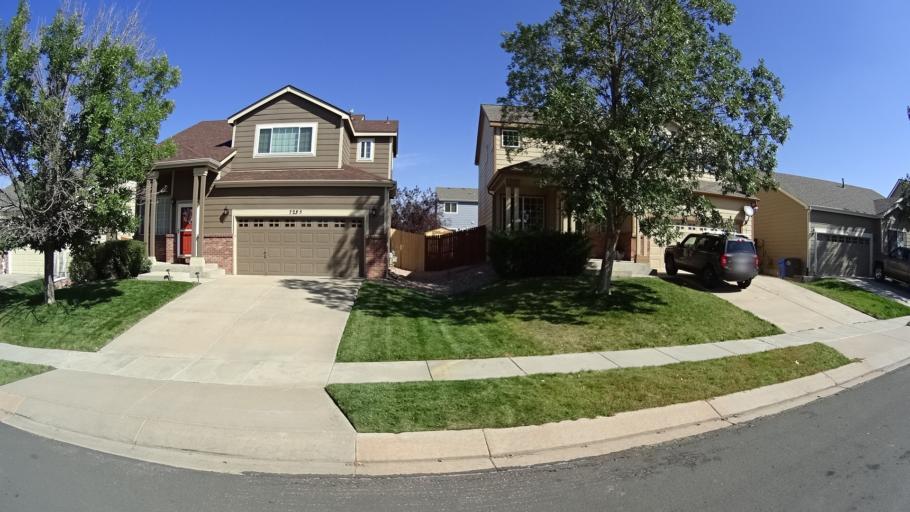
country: US
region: Colorado
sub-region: El Paso County
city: Cimarron Hills
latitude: 38.8851
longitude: -104.6934
